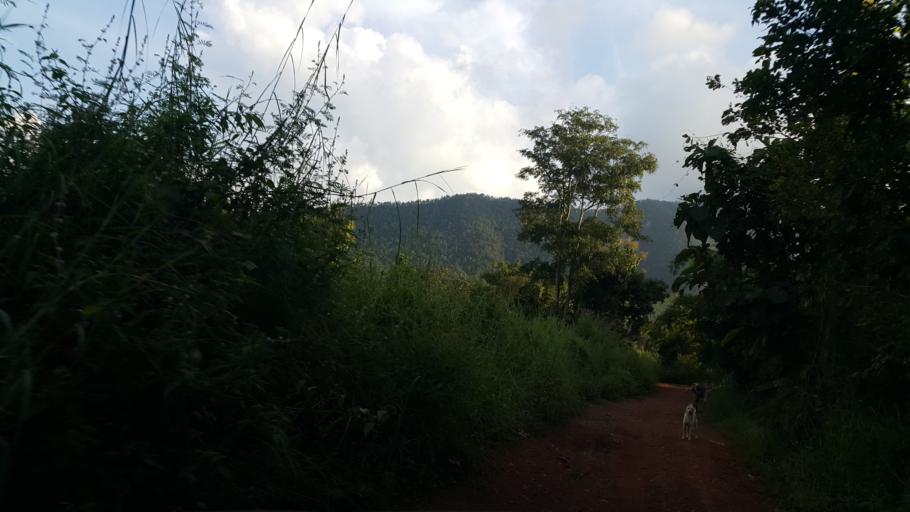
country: TH
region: Chiang Mai
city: Mae On
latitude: 18.7426
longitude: 99.2480
